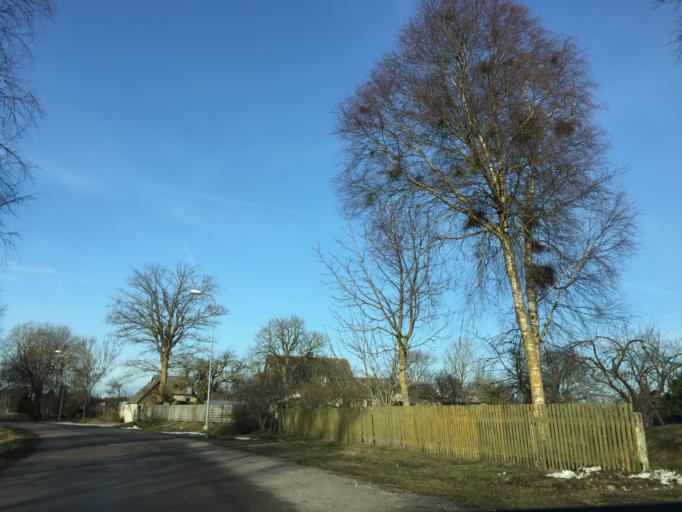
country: EE
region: Saare
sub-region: Kuressaare linn
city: Kuressaare
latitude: 58.3658
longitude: 22.0335
